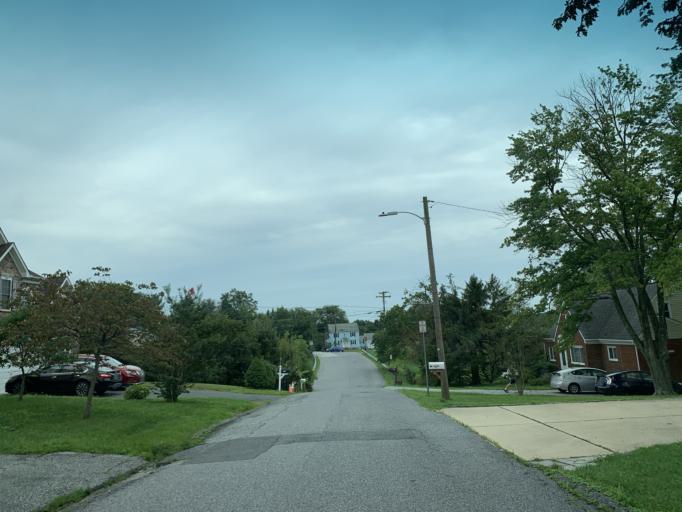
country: US
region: Maryland
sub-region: Baltimore County
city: Carney
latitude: 39.4086
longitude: -76.5155
